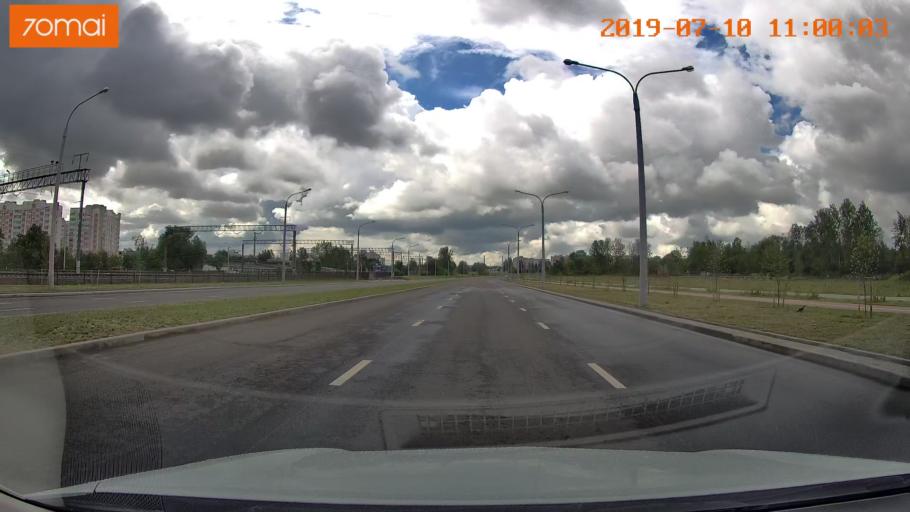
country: BY
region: Minsk
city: Minsk
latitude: 53.8623
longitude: 27.5588
